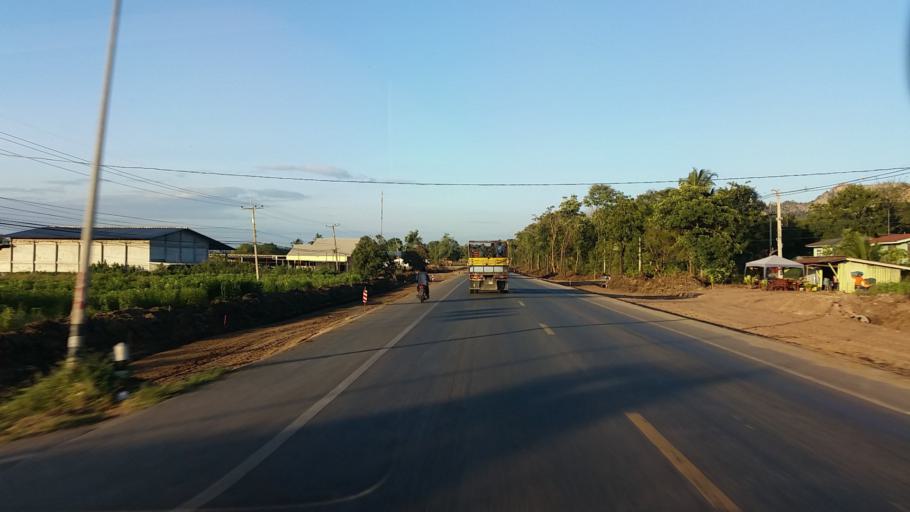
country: TH
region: Lop Buri
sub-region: Amphoe Lam Sonthi
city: Lam Sonthi
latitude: 15.2458
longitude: 101.2973
